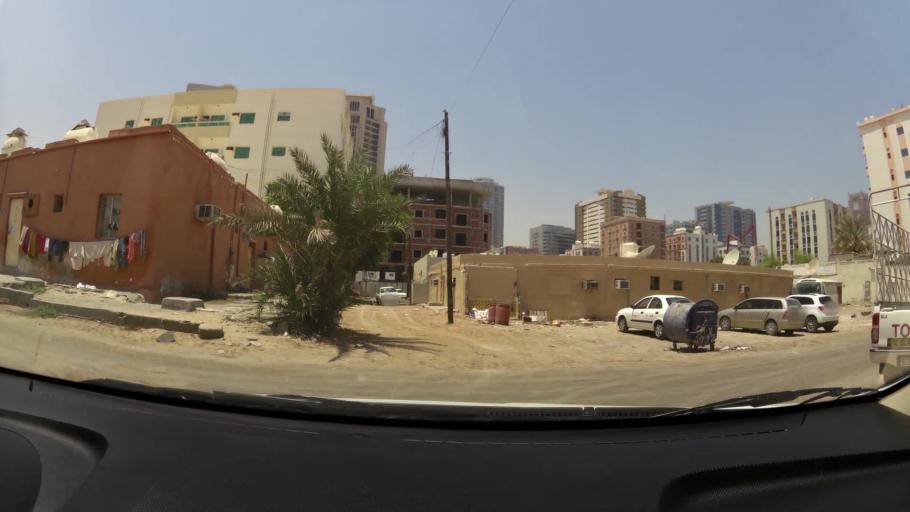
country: AE
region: Ajman
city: Ajman
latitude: 25.3953
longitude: 55.4391
